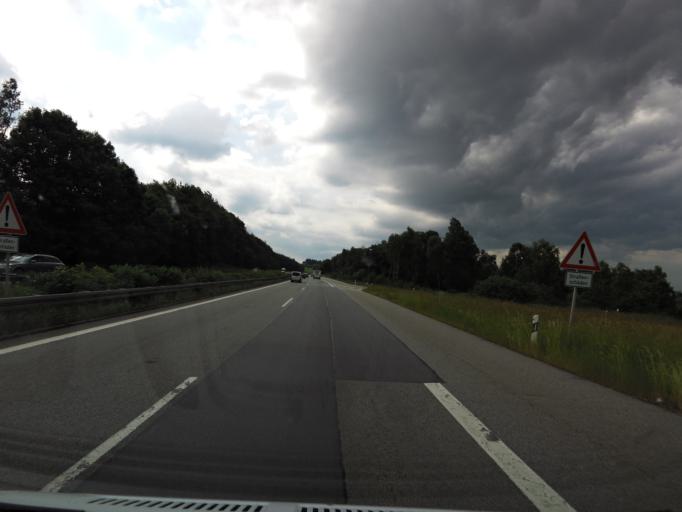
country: DE
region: Bavaria
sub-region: Lower Bavaria
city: Aussernzell
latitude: 48.6865
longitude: 13.2112
